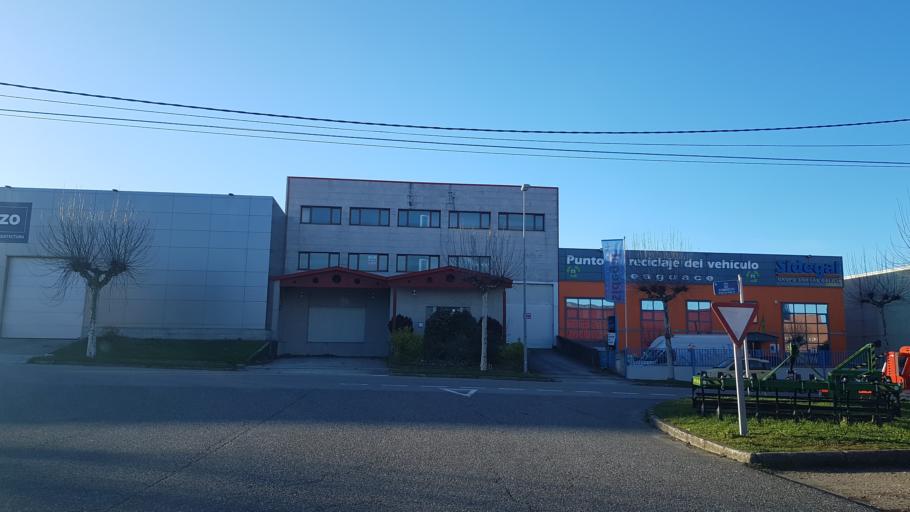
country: ES
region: Galicia
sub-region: Provincia de Lugo
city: Lugo
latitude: 43.0472
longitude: -7.5631
